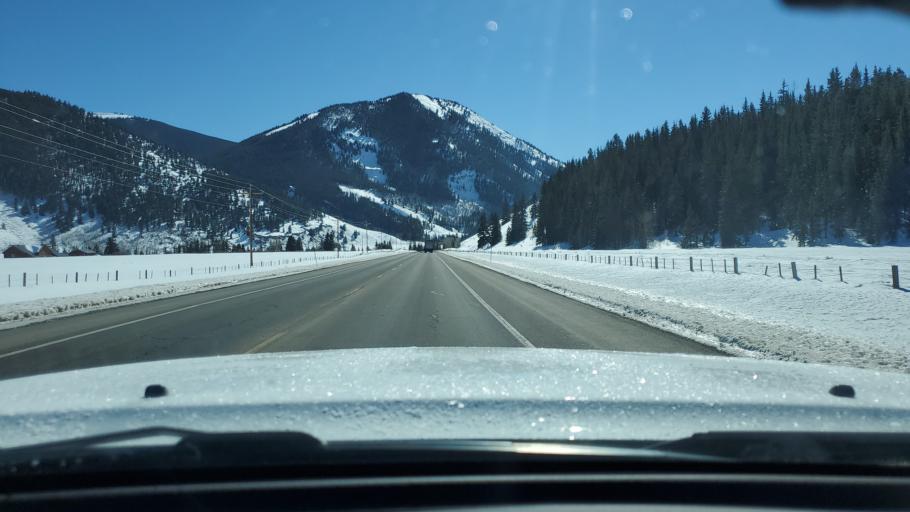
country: US
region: Colorado
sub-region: Gunnison County
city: Crested Butte
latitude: 38.8002
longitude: -106.8842
